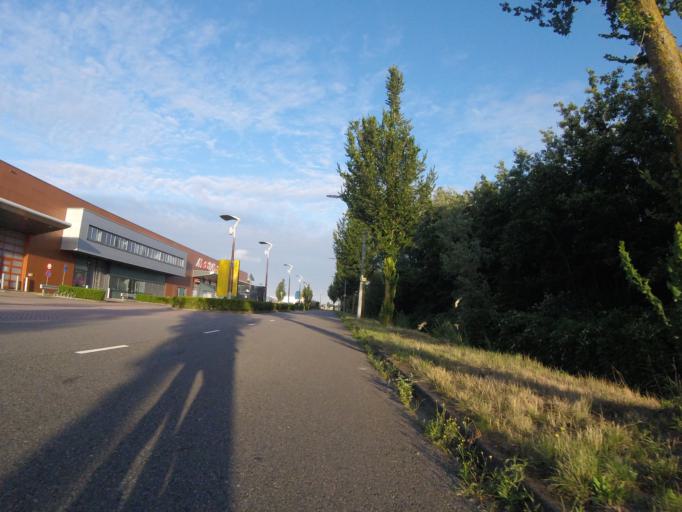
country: NL
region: North Holland
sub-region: Gemeente Heemstede
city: Heemstede
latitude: 52.3310
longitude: 4.6275
